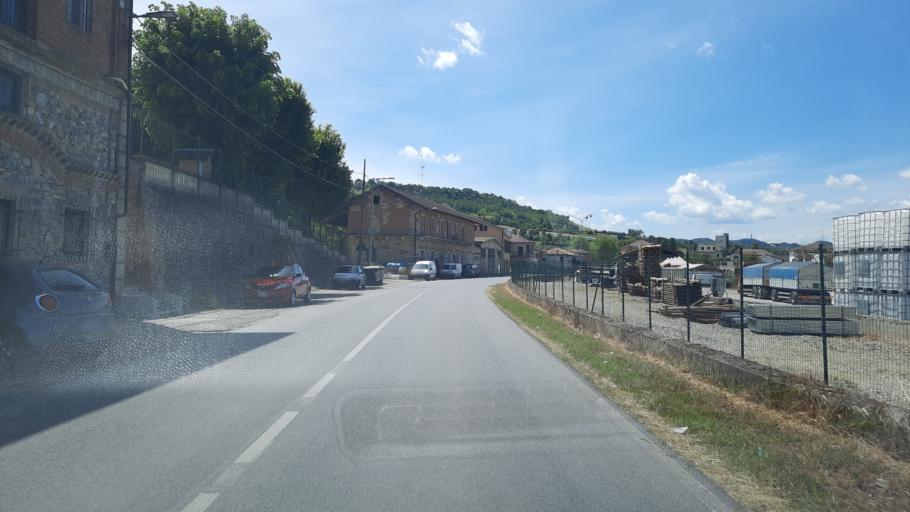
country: IT
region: Piedmont
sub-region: Provincia di Asti
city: Moncalvo
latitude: 45.0594
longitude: 8.2643
